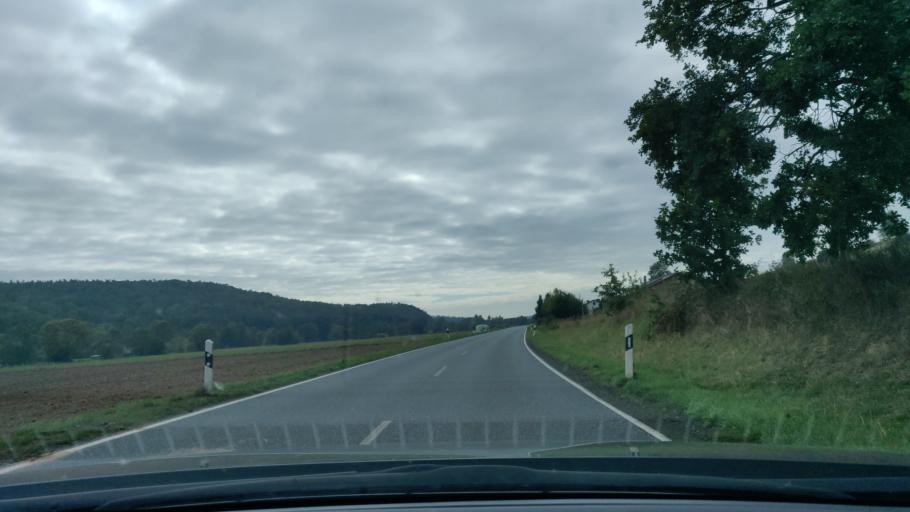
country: DE
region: Hesse
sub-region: Regierungsbezirk Kassel
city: Neuental
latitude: 50.9924
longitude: 9.2078
